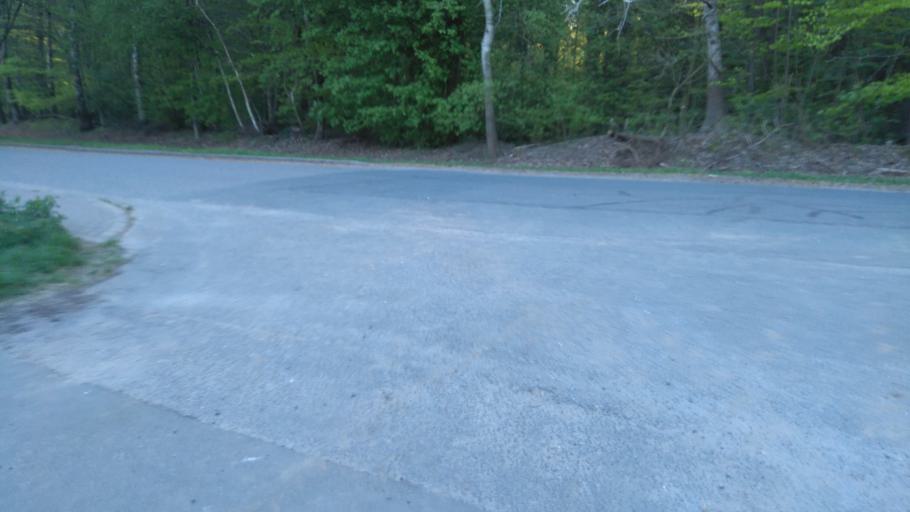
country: DE
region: Lower Saxony
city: Nottensdorf
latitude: 53.4749
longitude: 9.6162
